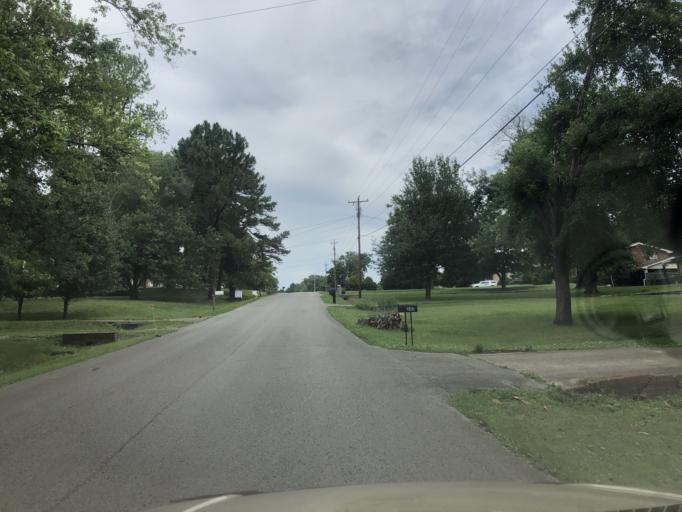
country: US
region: Tennessee
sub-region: Davidson County
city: Lakewood
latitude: 36.2533
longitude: -86.6101
